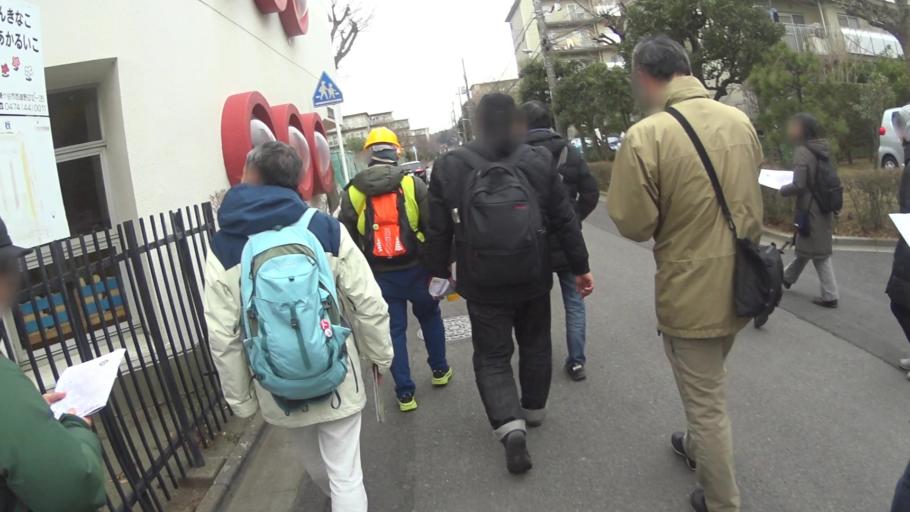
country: JP
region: Chiba
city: Funabashi
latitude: 35.7498
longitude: 139.9843
